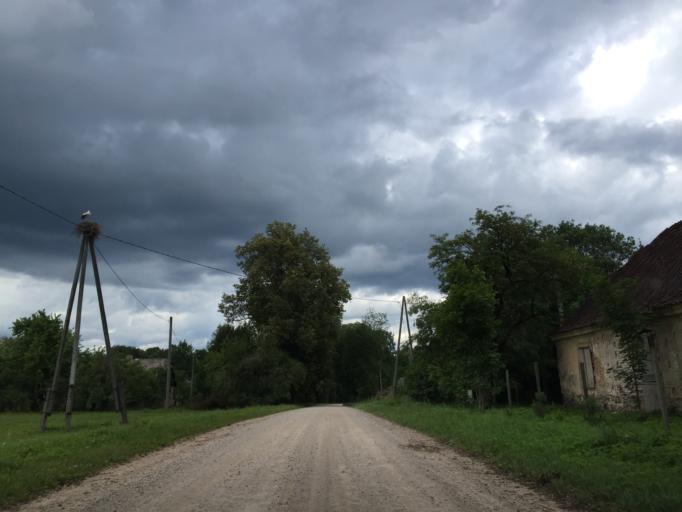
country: LV
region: Malpils
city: Malpils
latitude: 56.9278
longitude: 25.0099
